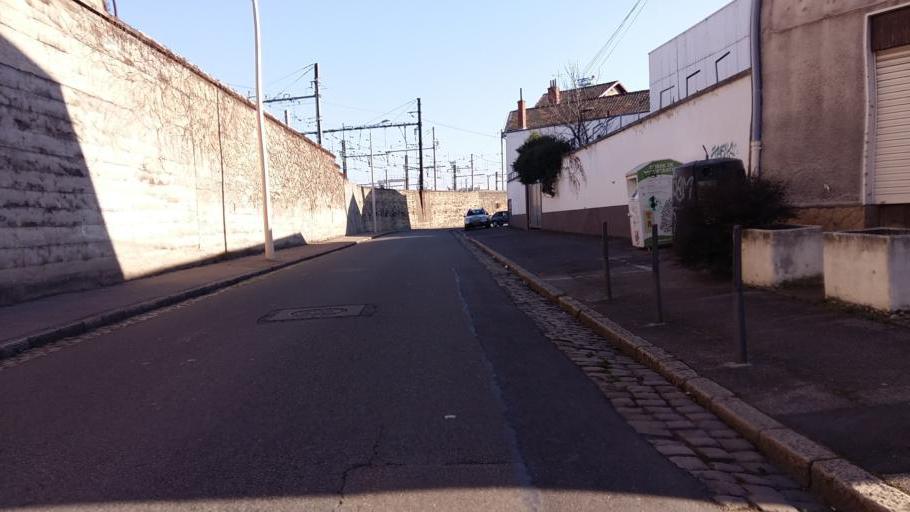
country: FR
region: Rhone-Alpes
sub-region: Departement du Rhone
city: Lyon
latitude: 45.7416
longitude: 4.8443
